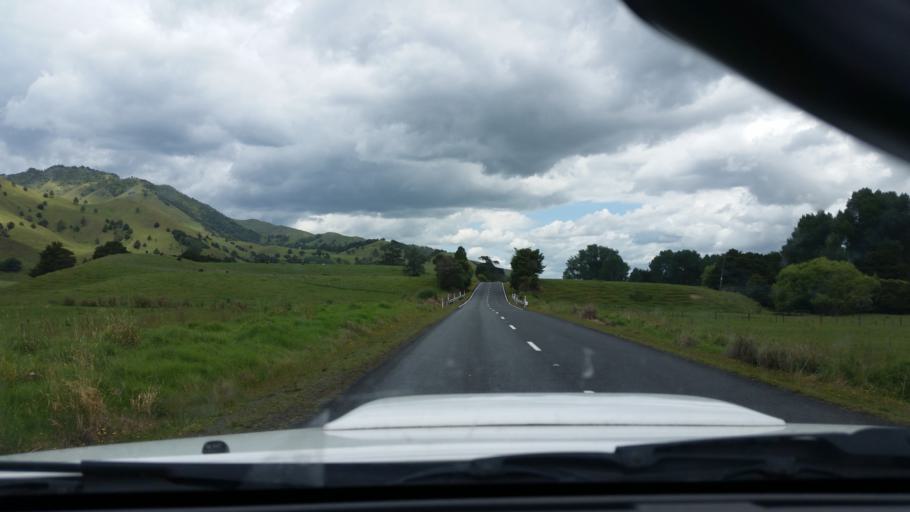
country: NZ
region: Northland
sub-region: Kaipara District
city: Dargaville
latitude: -35.7909
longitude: 173.9136
